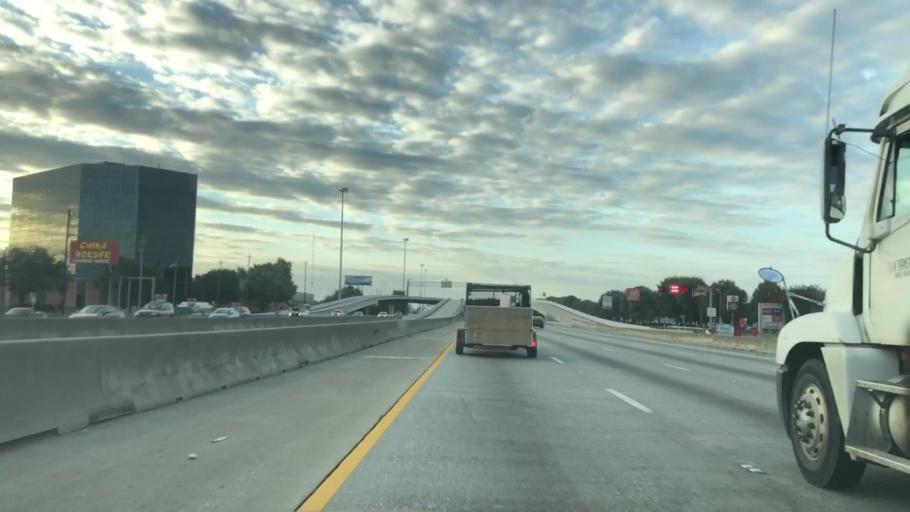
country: US
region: Texas
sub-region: Harris County
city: Aldine
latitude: 29.9227
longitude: -95.4124
